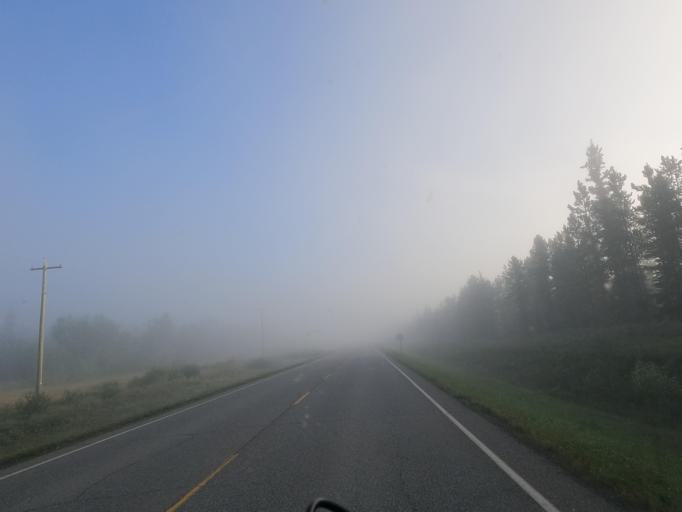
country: CA
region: Yukon
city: Whitehorse
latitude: 60.8878
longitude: -135.1842
